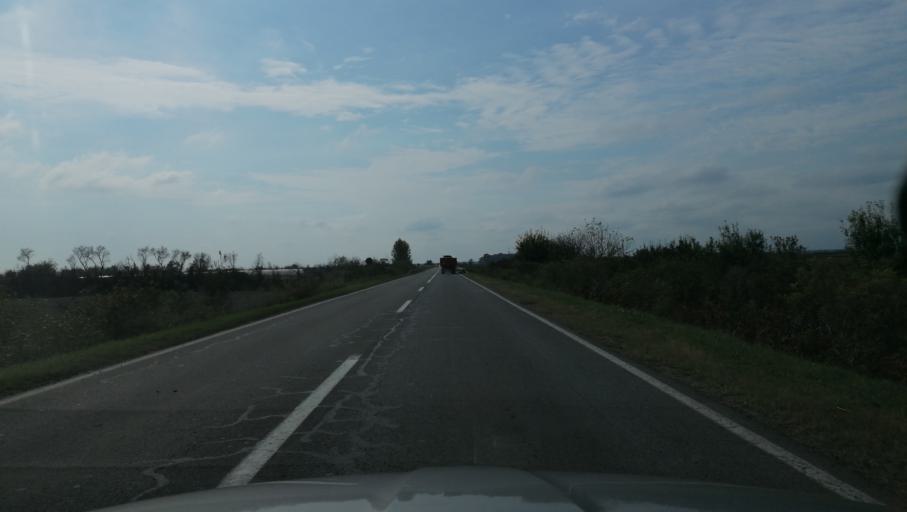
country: RS
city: Ravnje
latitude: 45.0087
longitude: 19.3920
